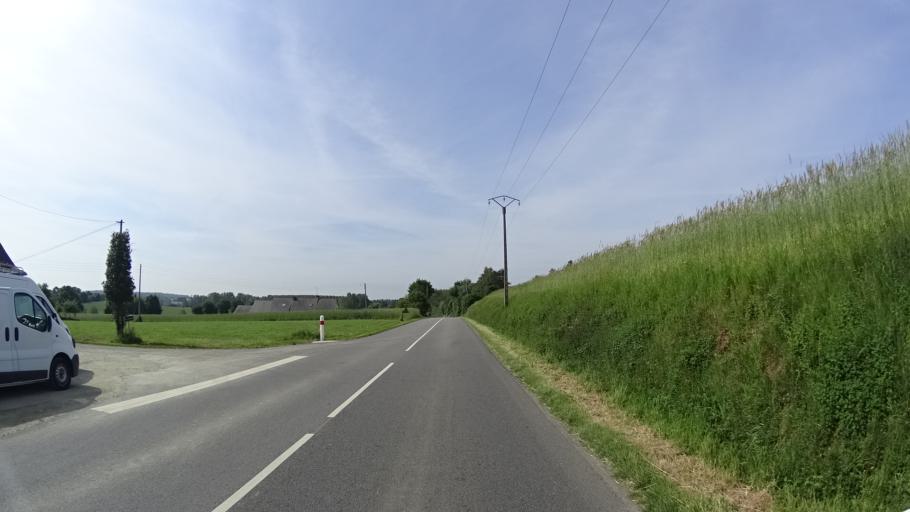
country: FR
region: Brittany
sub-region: Departement d'Ille-et-Vilaine
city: Chateaugiron
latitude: 48.0282
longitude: -1.5055
